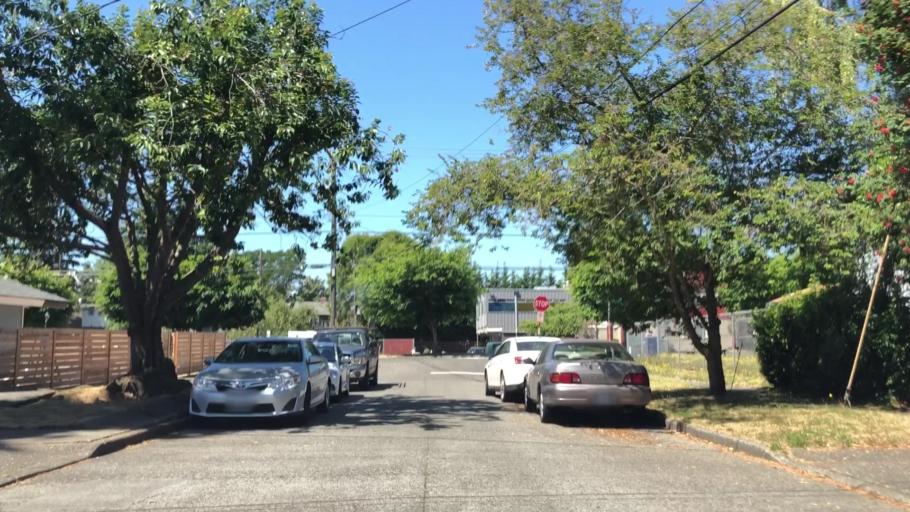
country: US
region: Washington
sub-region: King County
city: Shoreline
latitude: 47.6920
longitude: -122.3493
